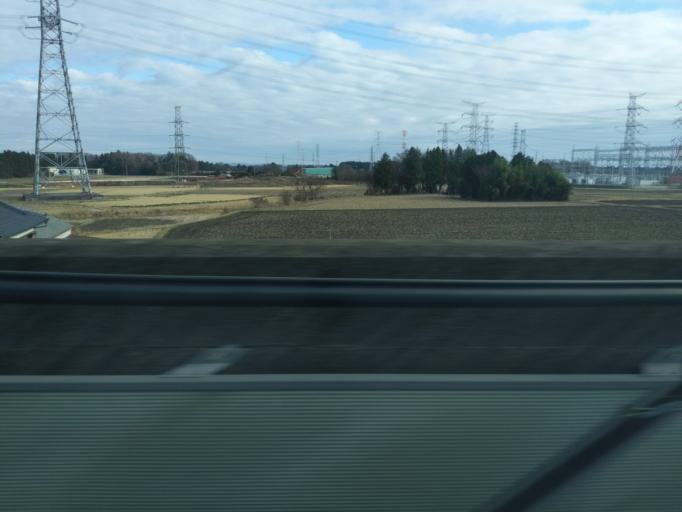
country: JP
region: Tochigi
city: Ujiie
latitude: 36.6594
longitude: 139.9138
